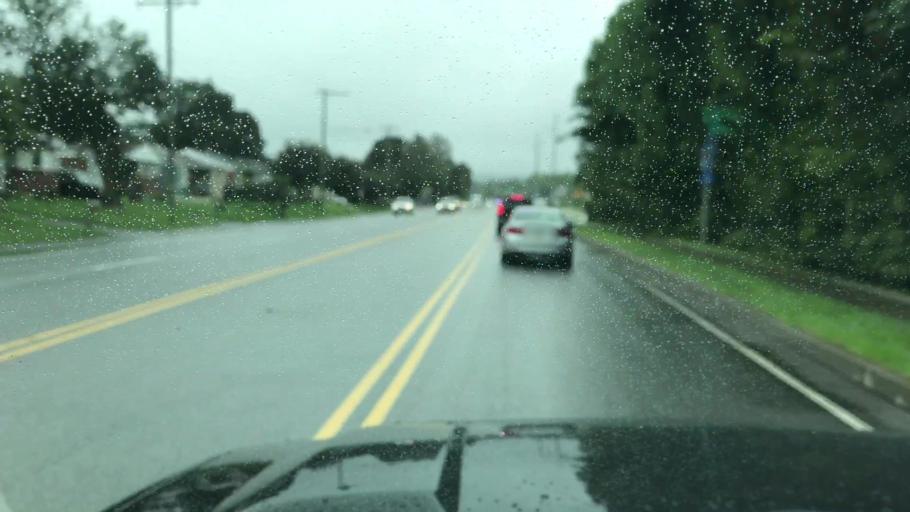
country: US
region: Pennsylvania
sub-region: York County
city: East York
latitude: 39.9763
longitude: -76.6945
